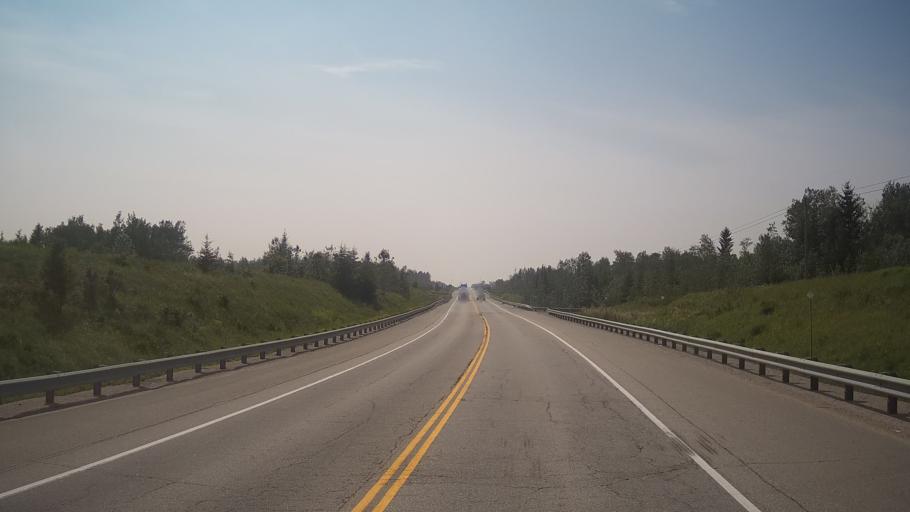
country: CA
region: Ontario
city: Kapuskasing
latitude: 49.2894
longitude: -81.7820
